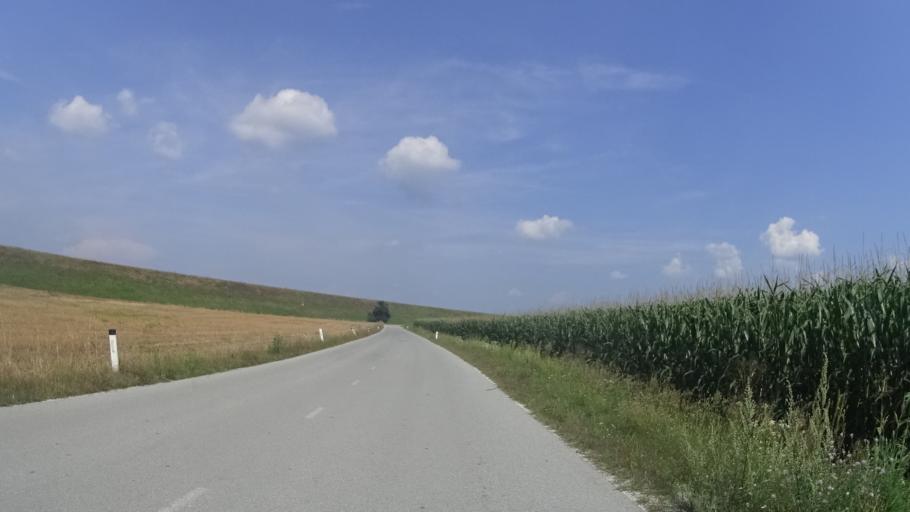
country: SI
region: Starse
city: Starse
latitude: 46.4465
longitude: 15.7769
